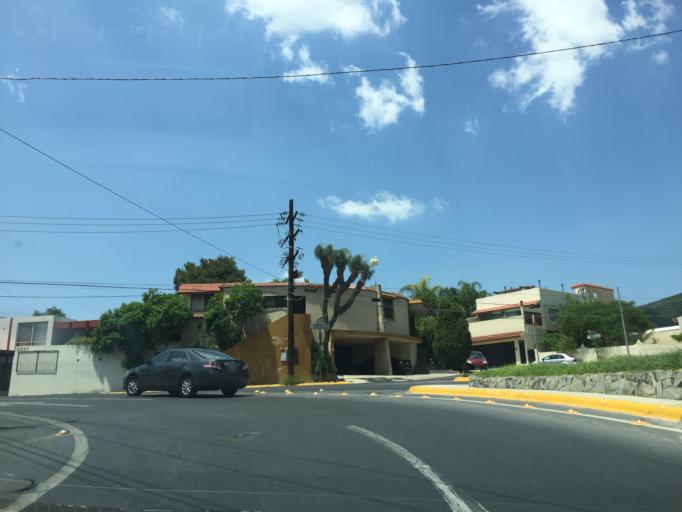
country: MX
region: Nuevo Leon
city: Guadalupe
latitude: 25.6398
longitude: -100.2677
